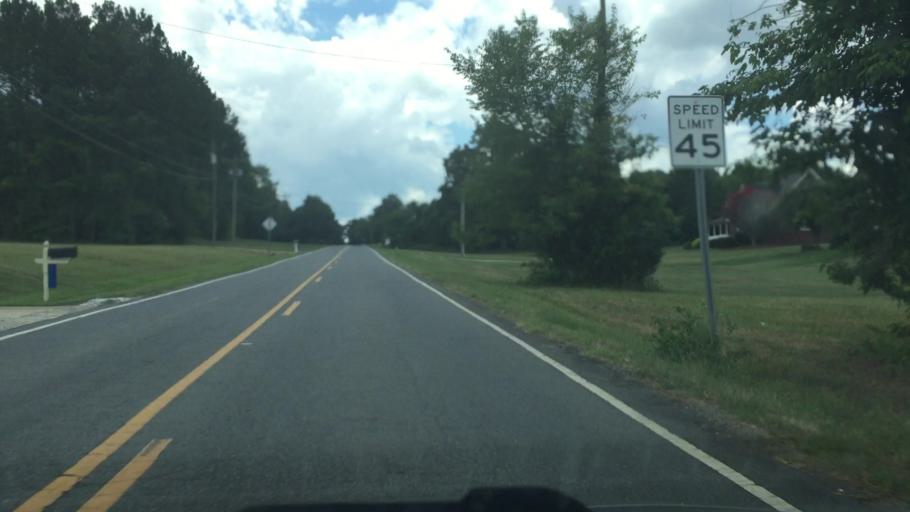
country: US
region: North Carolina
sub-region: Rowan County
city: Enochville
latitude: 35.4650
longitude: -80.7306
